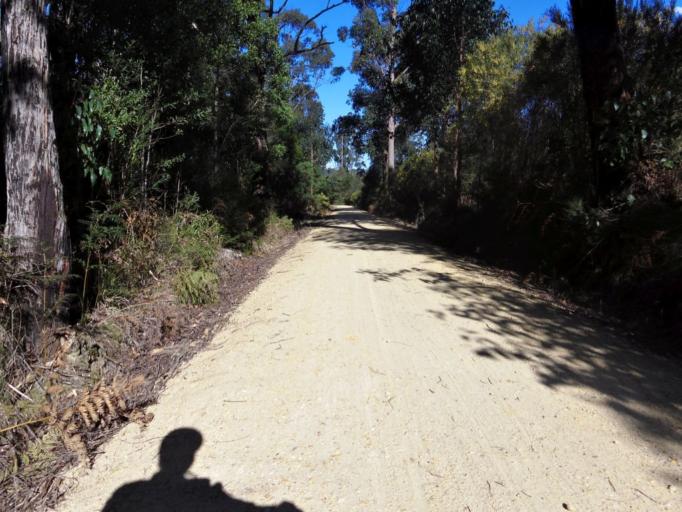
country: AU
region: Victoria
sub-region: Latrobe
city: Moe
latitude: -38.3723
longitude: 146.2163
